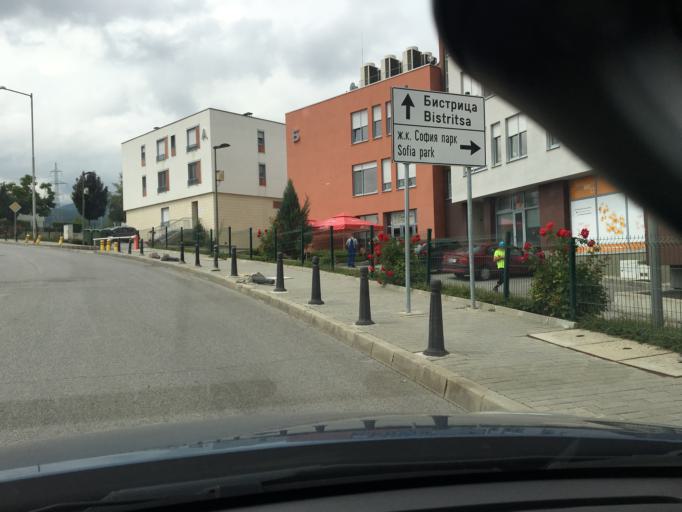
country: BG
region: Sofia-Capital
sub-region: Stolichna Obshtina
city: Sofia
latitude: 42.6206
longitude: 23.3694
